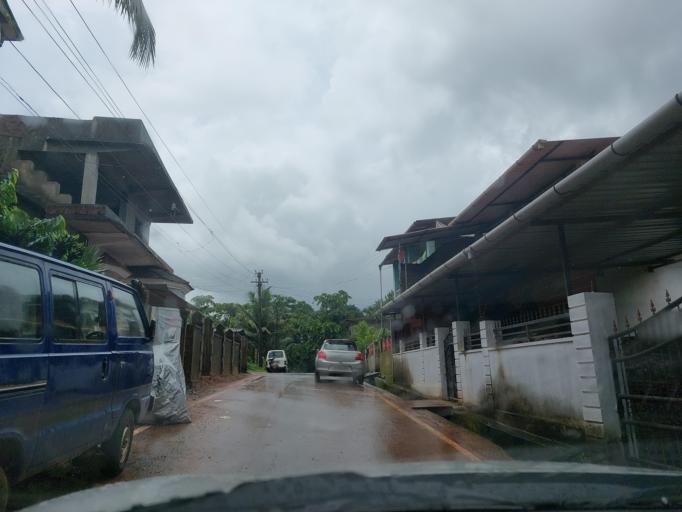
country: IN
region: Goa
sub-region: North Goa
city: Valpoy
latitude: 15.5328
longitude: 74.1301
